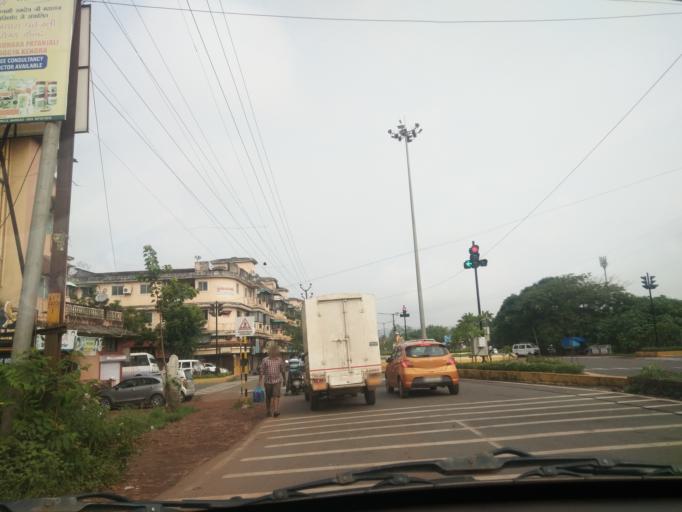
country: IN
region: Goa
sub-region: South Goa
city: Davorlim
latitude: 15.2855
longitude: 73.9789
